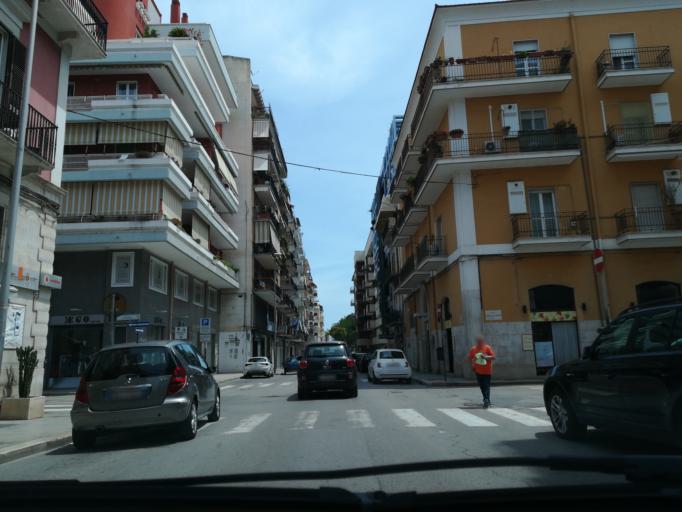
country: IT
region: Apulia
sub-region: Provincia di Barletta - Andria - Trani
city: Barletta
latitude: 41.3179
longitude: 16.2841
